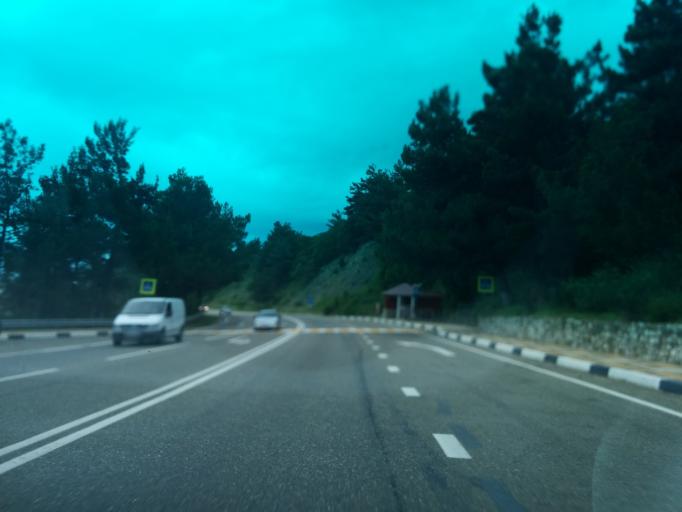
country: RU
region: Krasnodarskiy
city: Ol'ginka
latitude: 44.1837
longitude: 38.9262
